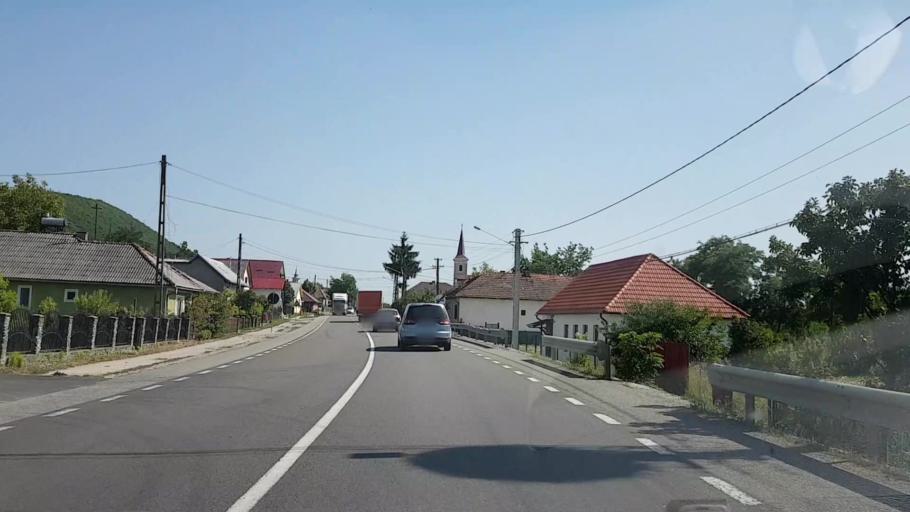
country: RO
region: Bistrita-Nasaud
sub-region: Comuna Sieu-Odorhei
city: Sieu-Odorhei
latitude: 47.1485
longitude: 24.3057
